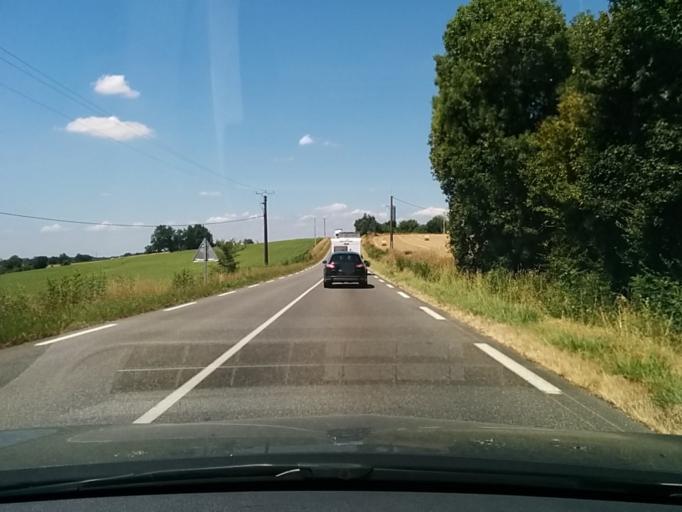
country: FR
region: Midi-Pyrenees
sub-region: Departement du Gers
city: Eauze
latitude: 43.7749
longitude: 0.1242
